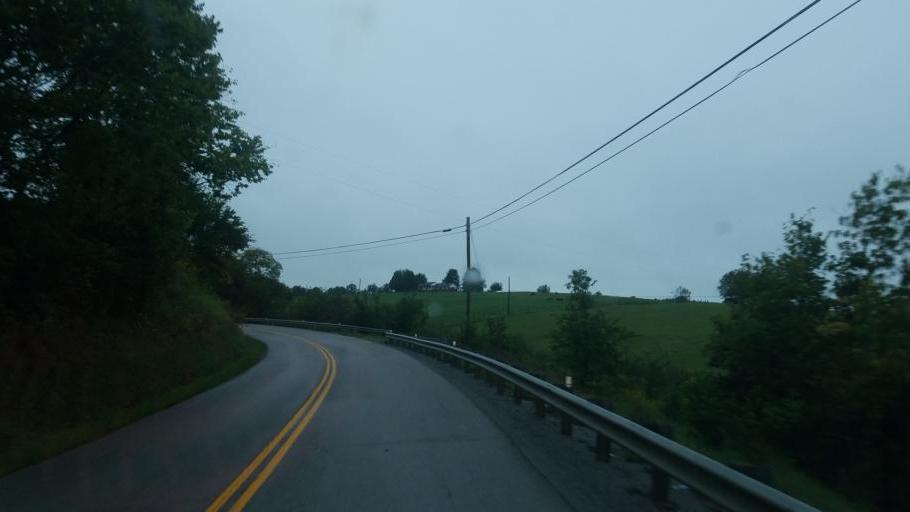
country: US
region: Kentucky
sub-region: Fleming County
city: Flemingsburg
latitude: 38.4171
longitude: -83.6968
